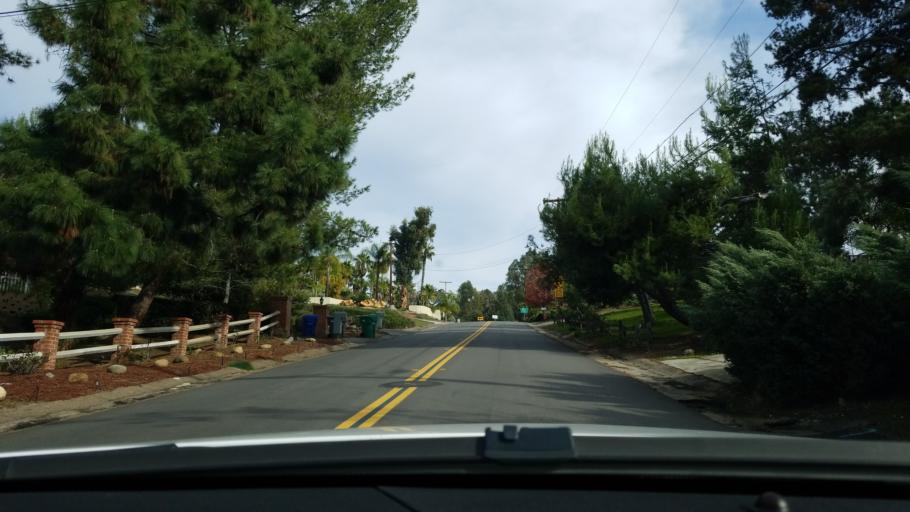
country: US
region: California
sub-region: San Diego County
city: Casa de Oro-Mount Helix
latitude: 32.7702
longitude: -116.9575
